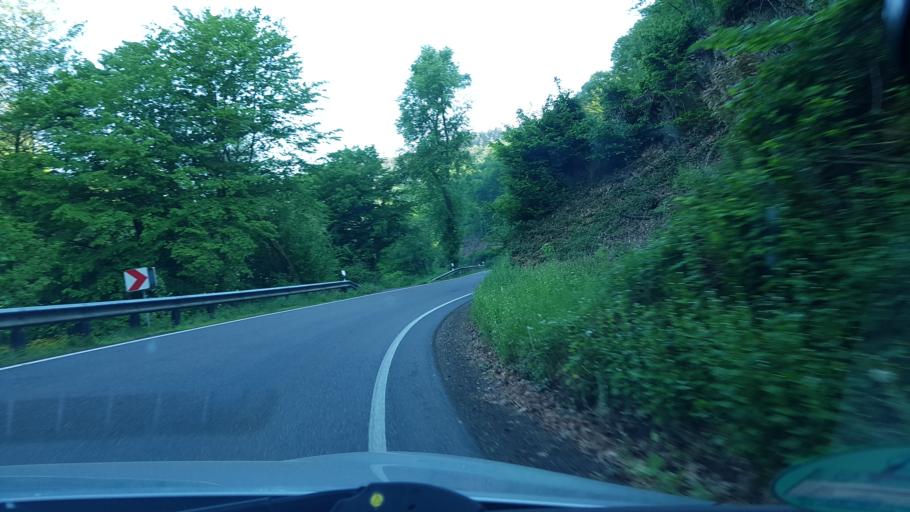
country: DE
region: Rheinland-Pfalz
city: Kadenbach
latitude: 50.3748
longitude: 7.7382
